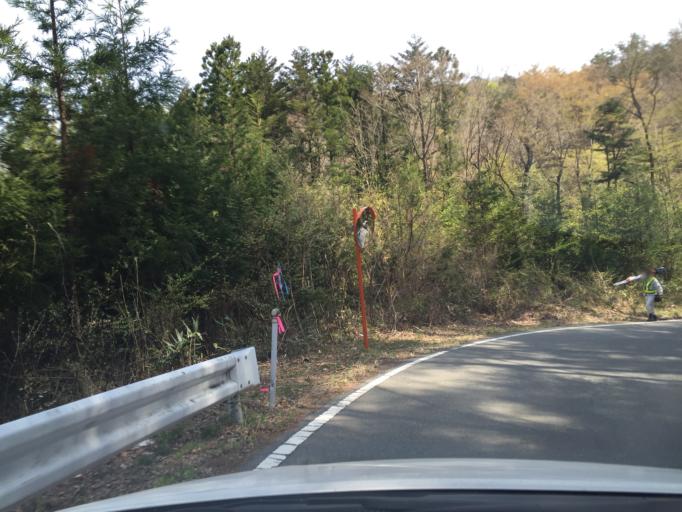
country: JP
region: Fukushima
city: Iwaki
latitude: 37.2581
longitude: 140.8389
